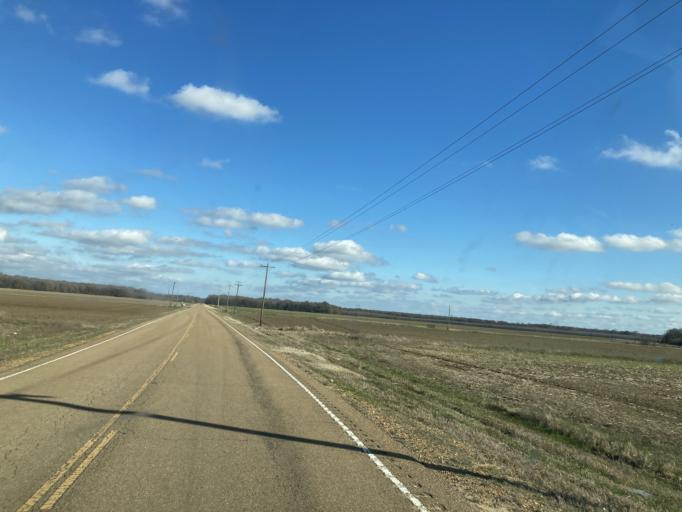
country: US
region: Mississippi
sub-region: Yazoo County
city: Yazoo City
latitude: 32.9618
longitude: -90.4919
